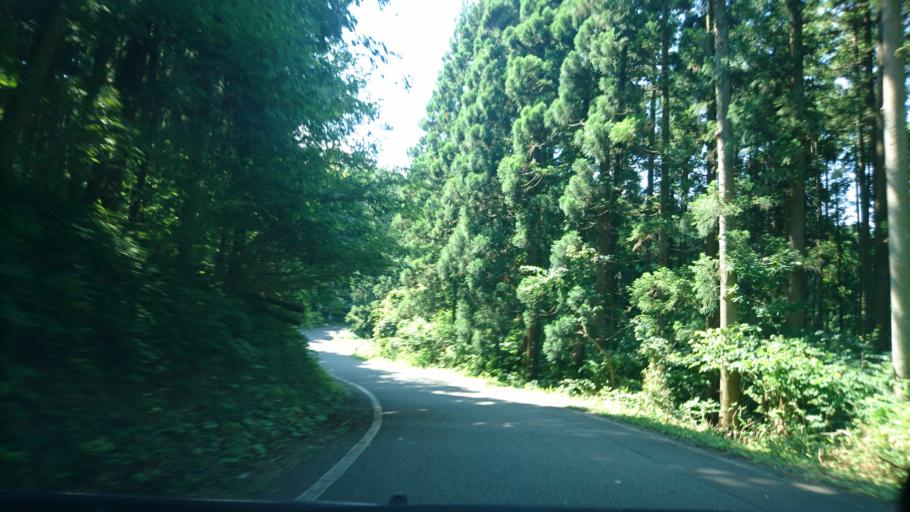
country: JP
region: Iwate
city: Ichinoseki
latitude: 38.9715
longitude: 141.1945
